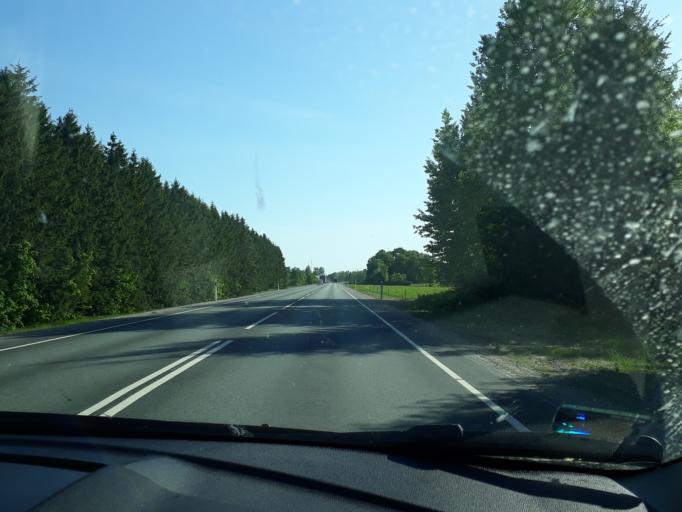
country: EE
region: Paernumaa
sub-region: Tootsi vald
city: Tootsi
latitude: 58.5427
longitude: 24.8430
